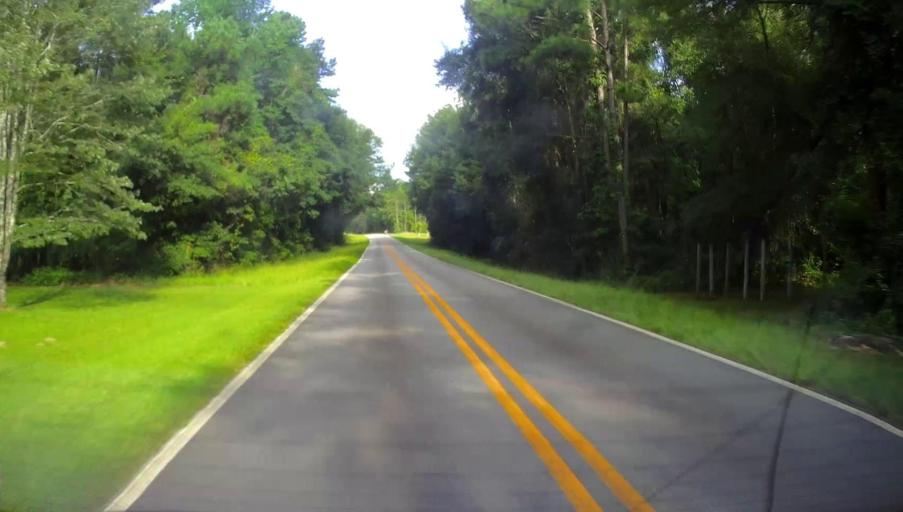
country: US
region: Georgia
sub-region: Crawford County
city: Knoxville
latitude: 32.7579
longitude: -83.9480
